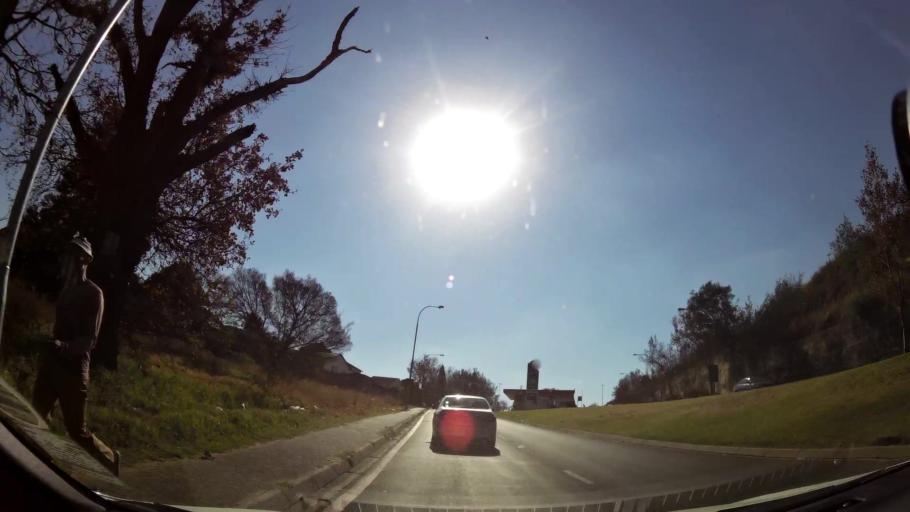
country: ZA
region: Gauteng
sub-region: City of Johannesburg Metropolitan Municipality
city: Johannesburg
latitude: -26.2615
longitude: 28.0583
